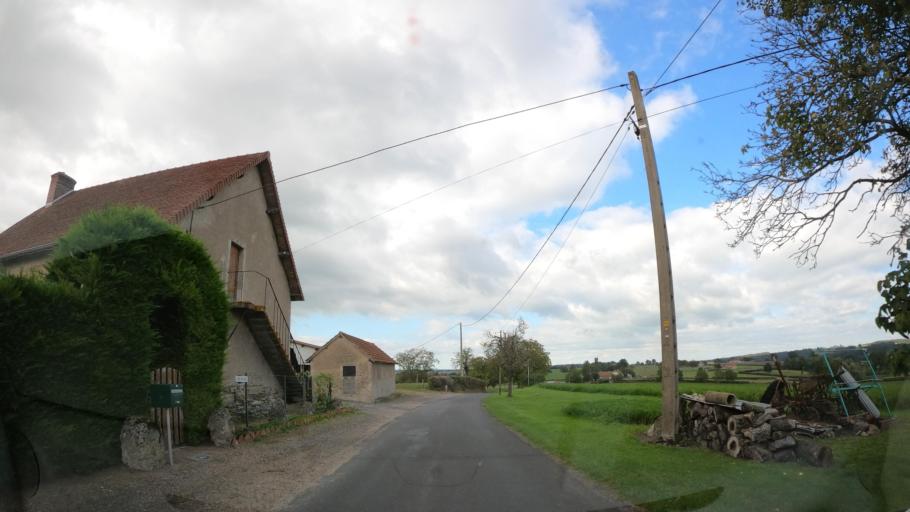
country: FR
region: Auvergne
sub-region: Departement de l'Allier
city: Lapalisse
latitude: 46.3646
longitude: 3.6212
